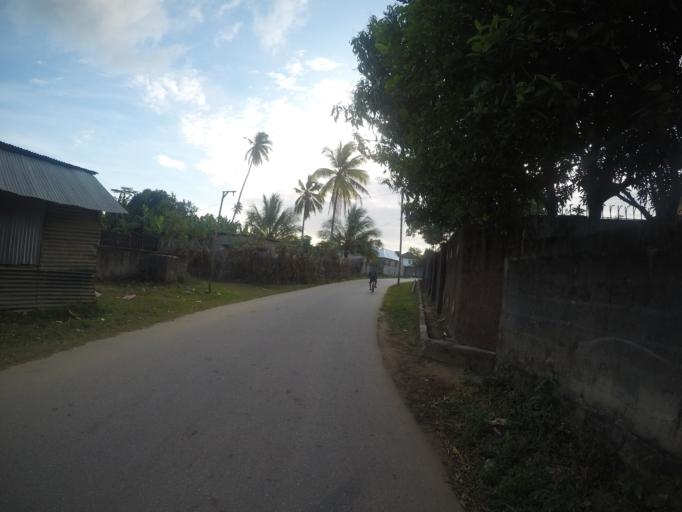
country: TZ
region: Zanzibar Central/South
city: Koani
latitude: -6.1950
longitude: 39.2627
